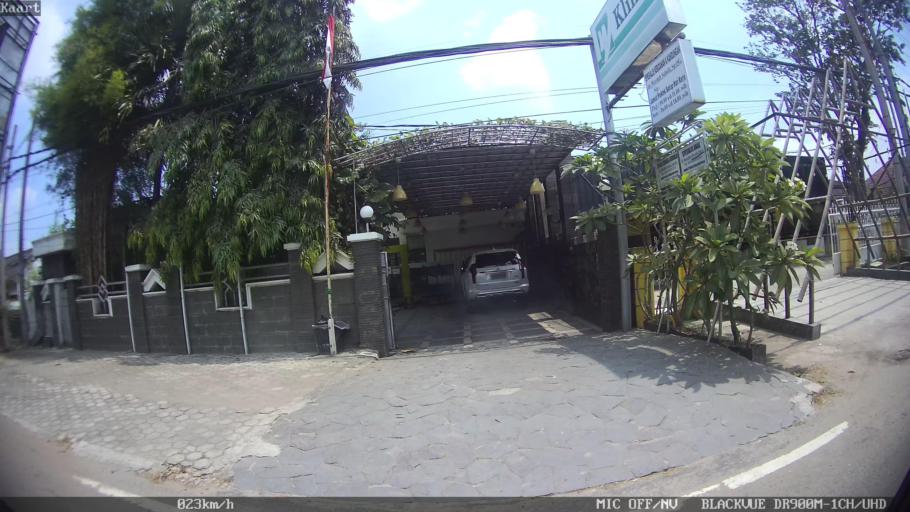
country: ID
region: Lampung
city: Kedaton
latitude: -5.3816
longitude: 105.2748
